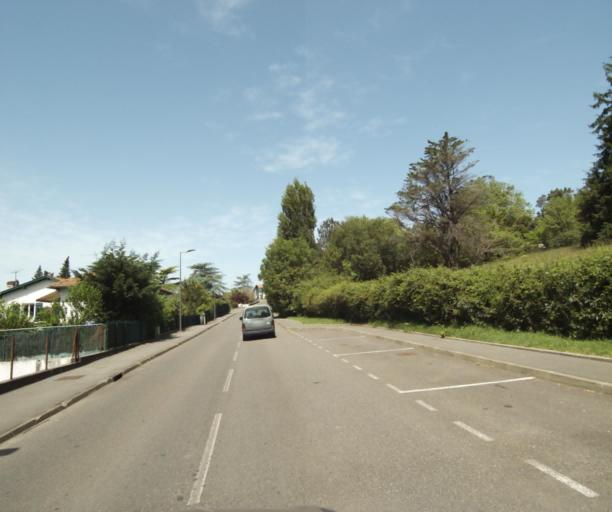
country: FR
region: Aquitaine
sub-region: Departement des Pyrenees-Atlantiques
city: Mouguerre
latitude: 43.4710
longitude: -1.4472
